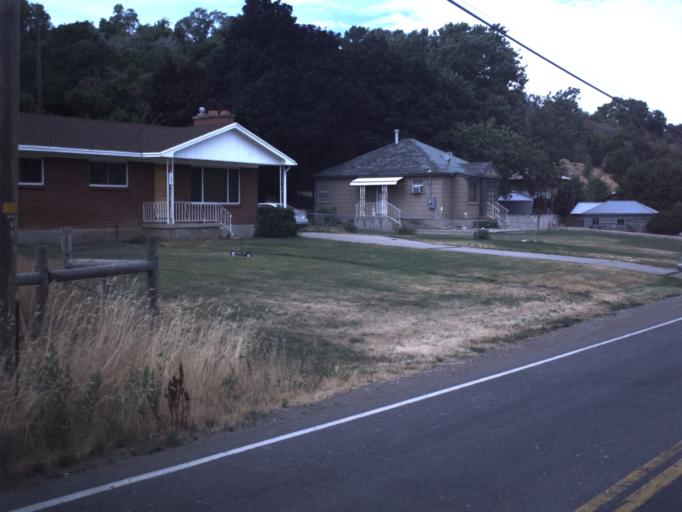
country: US
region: Utah
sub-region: Weber County
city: Washington Terrace
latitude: 41.1465
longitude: -111.9786
